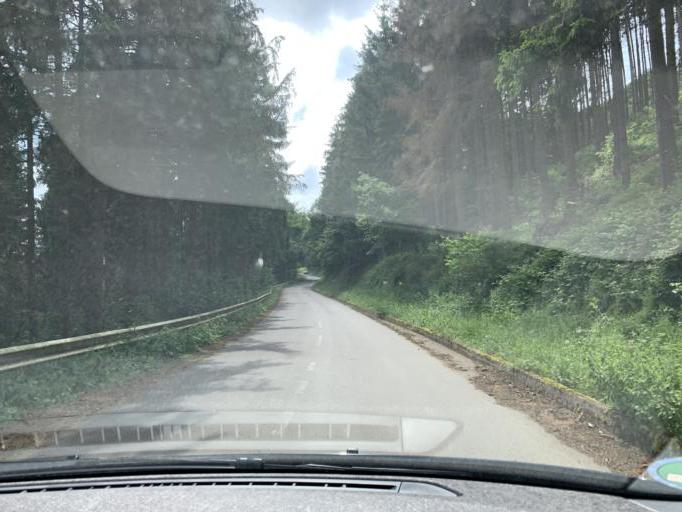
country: DE
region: North Rhine-Westphalia
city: Heimbach
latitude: 50.6534
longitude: 6.4102
